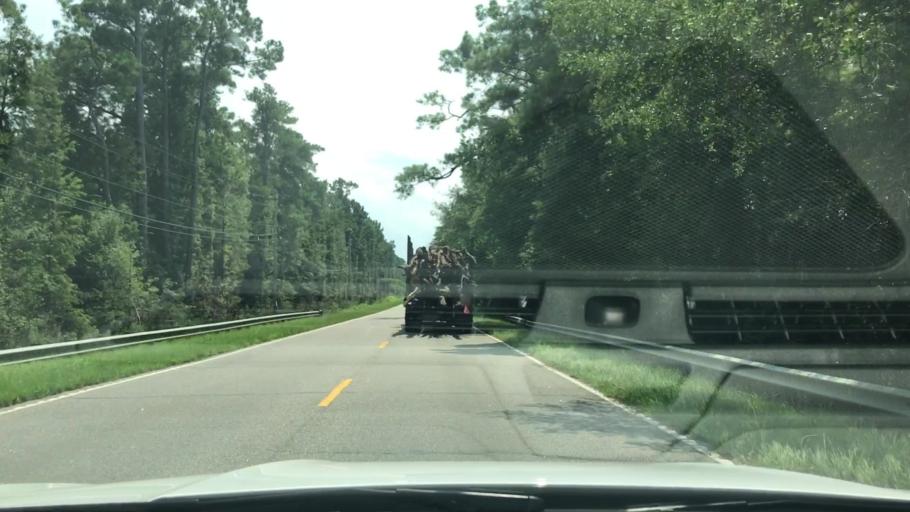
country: US
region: South Carolina
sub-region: Georgetown County
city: Georgetown
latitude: 33.4683
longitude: -79.2798
